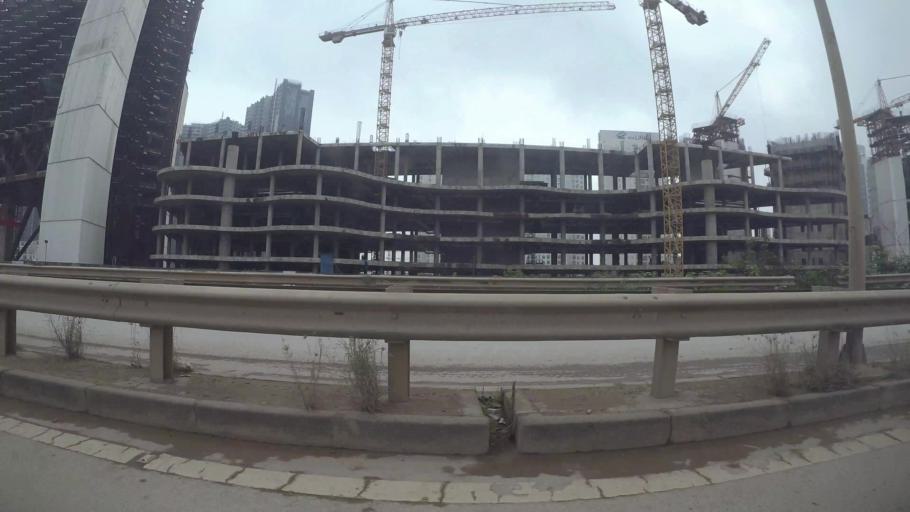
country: VN
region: Ha Noi
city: Tay Ho
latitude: 21.0824
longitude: 105.7893
